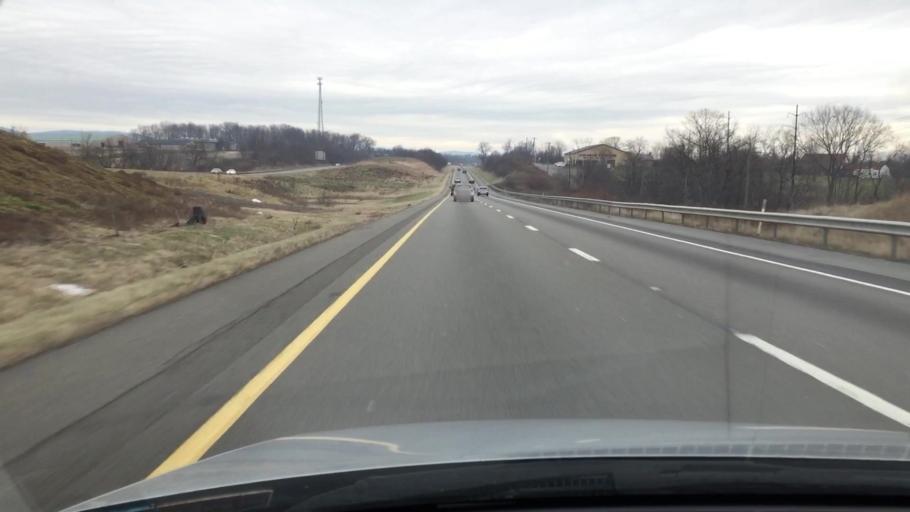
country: US
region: Pennsylvania
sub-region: Columbia County
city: Almedia
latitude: 41.0292
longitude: -76.3928
